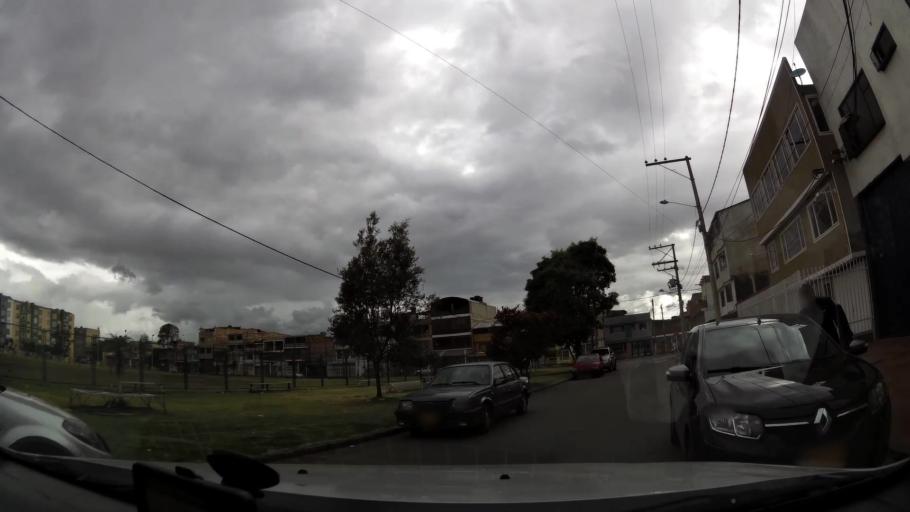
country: CO
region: Bogota D.C.
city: Bogota
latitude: 4.6111
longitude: -74.1355
